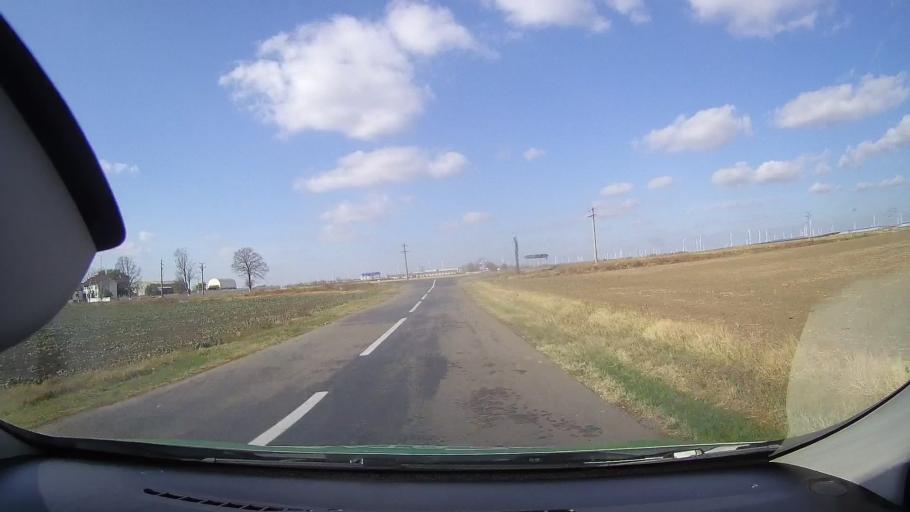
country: RO
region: Constanta
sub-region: Comuna Cogealac
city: Tariverde
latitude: 44.5586
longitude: 28.6120
